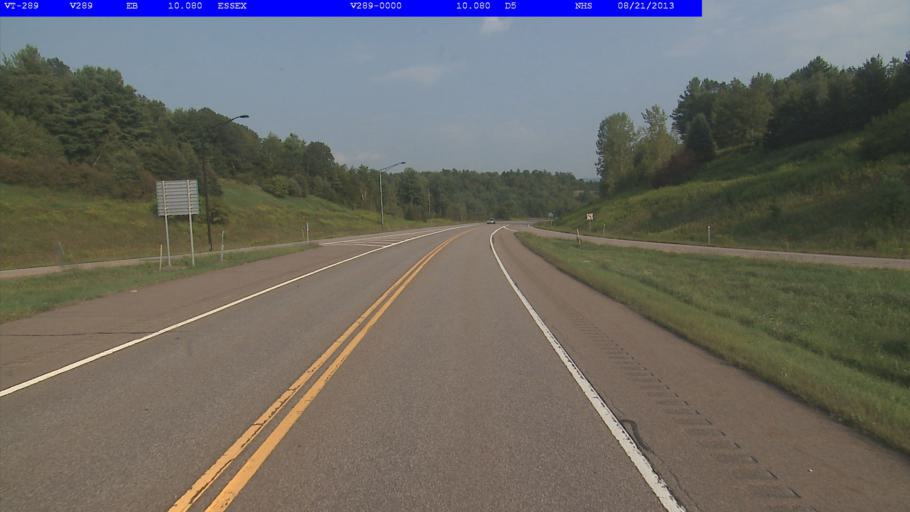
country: US
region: Vermont
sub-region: Chittenden County
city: Essex Junction
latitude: 44.5040
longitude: -73.0767
